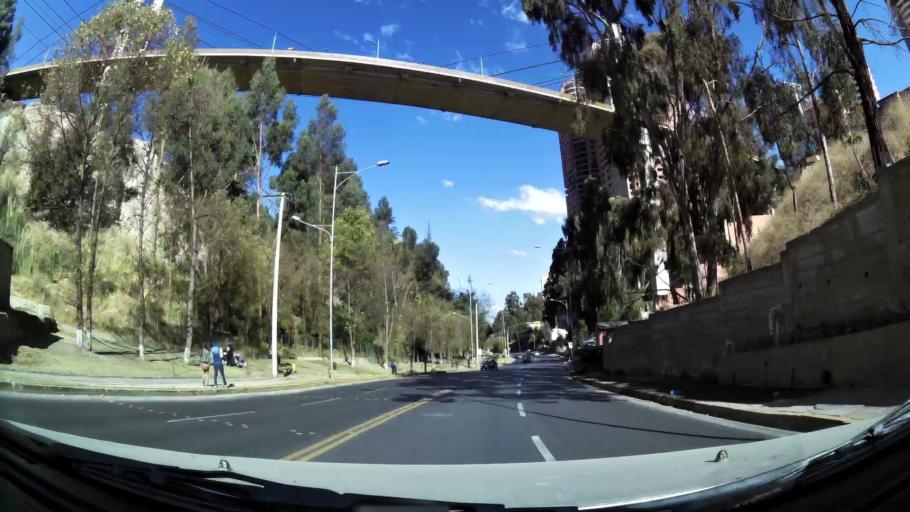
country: BO
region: La Paz
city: La Paz
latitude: -16.5073
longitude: -68.1232
